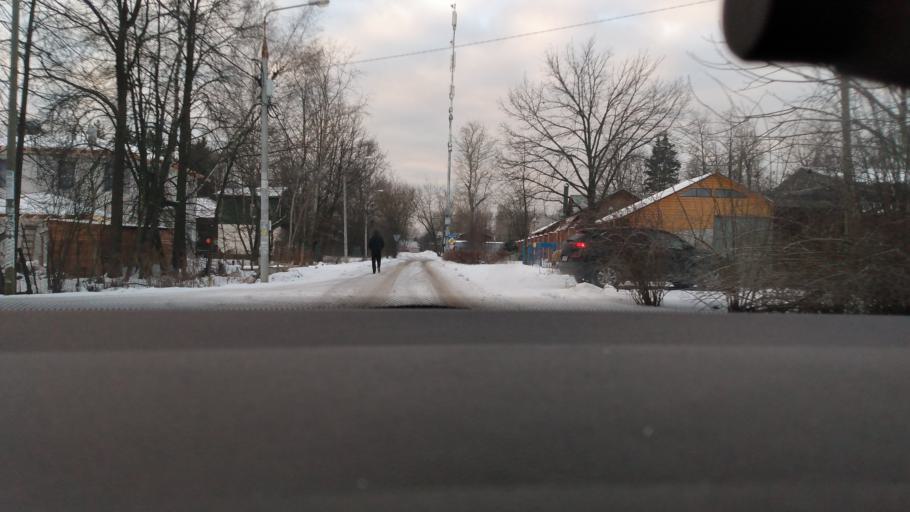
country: RU
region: Moskovskaya
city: Saltykovka
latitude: 55.7585
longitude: 37.9346
